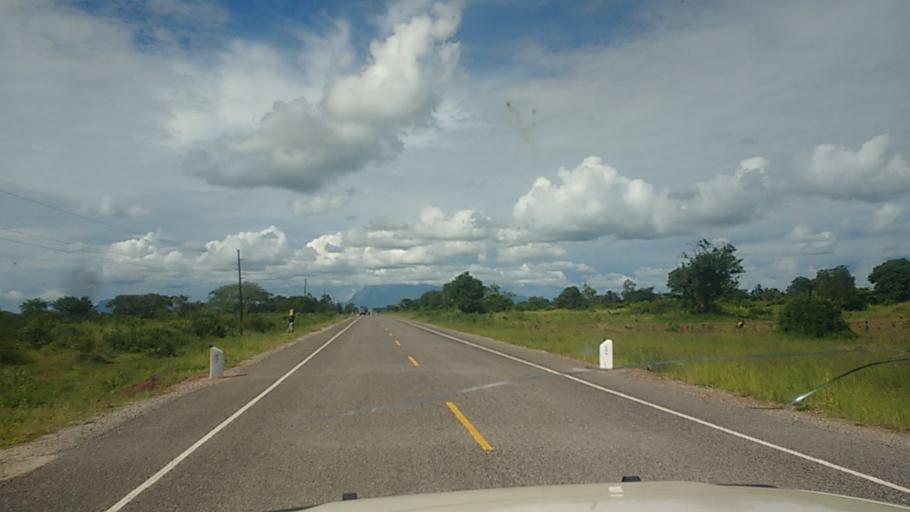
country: UG
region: Eastern Region
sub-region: Katakwi District
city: Katakwi
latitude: 1.9192
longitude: 34.0474
